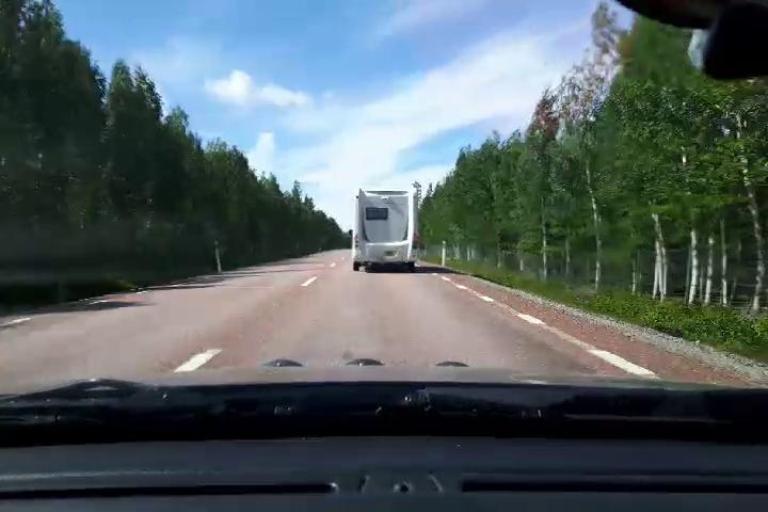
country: SE
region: Gaevleborg
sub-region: Bollnas Kommun
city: Kilafors
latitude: 61.2108
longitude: 16.7400
